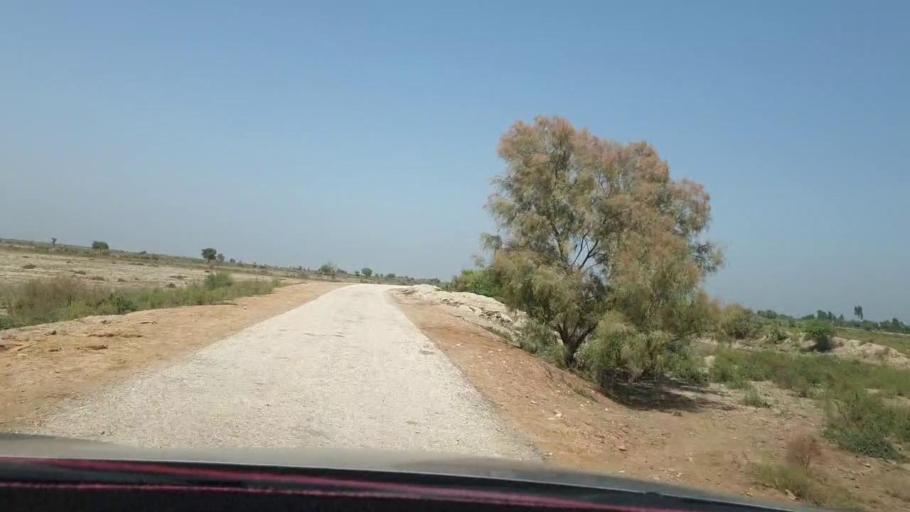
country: PK
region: Sindh
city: Warah
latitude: 27.5109
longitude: 67.7046
